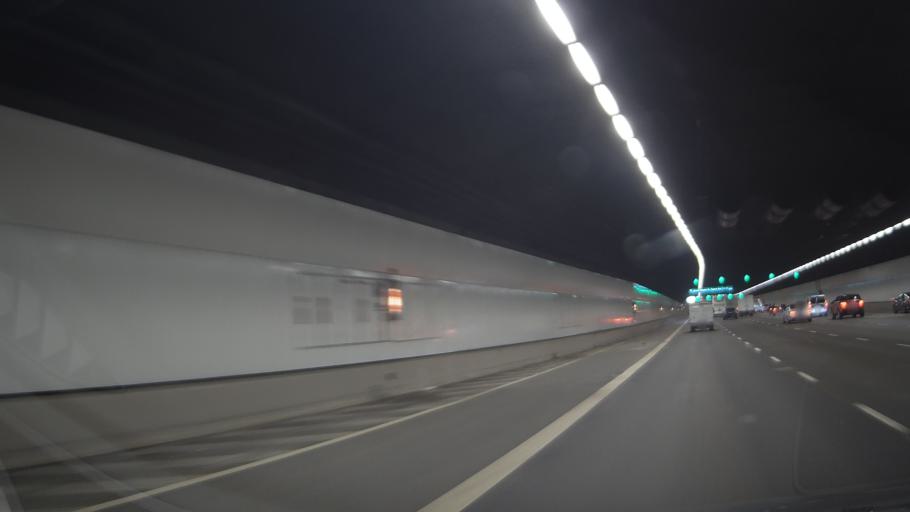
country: SG
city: Singapore
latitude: 1.2897
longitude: 103.8778
